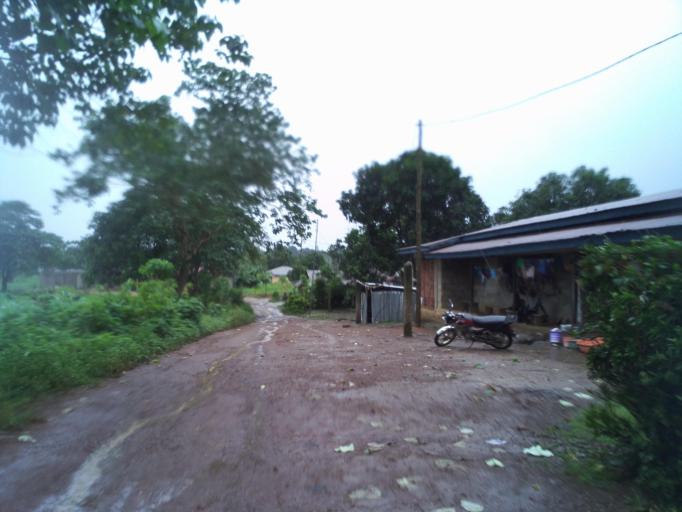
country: SL
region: Eastern Province
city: Kenema
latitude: 7.8562
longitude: -11.1929
